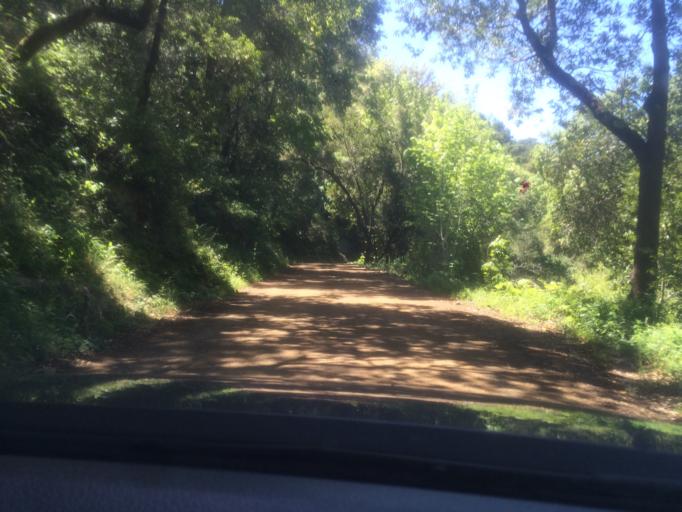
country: US
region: California
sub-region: San Luis Obispo County
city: Templeton
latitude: 35.5266
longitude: -120.7986
